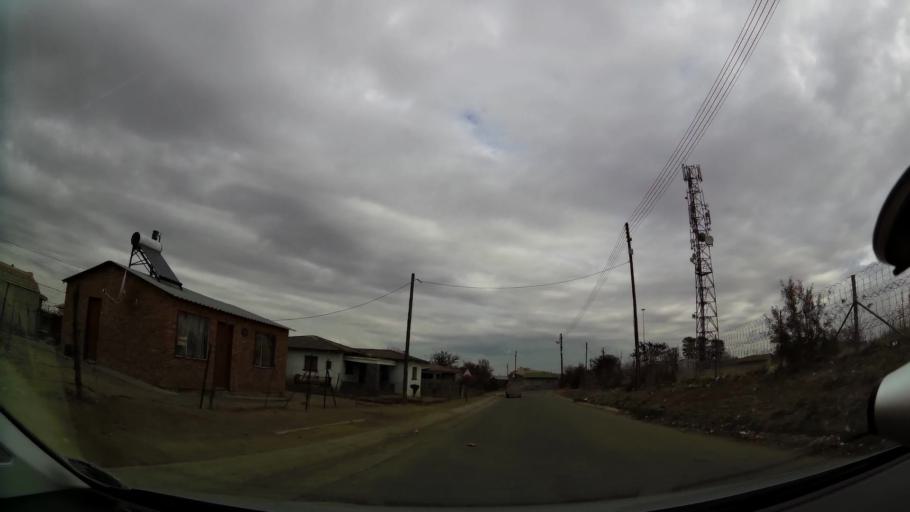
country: ZA
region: Orange Free State
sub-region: Fezile Dabi District Municipality
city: Kroonstad
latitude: -27.6497
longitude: 27.2038
